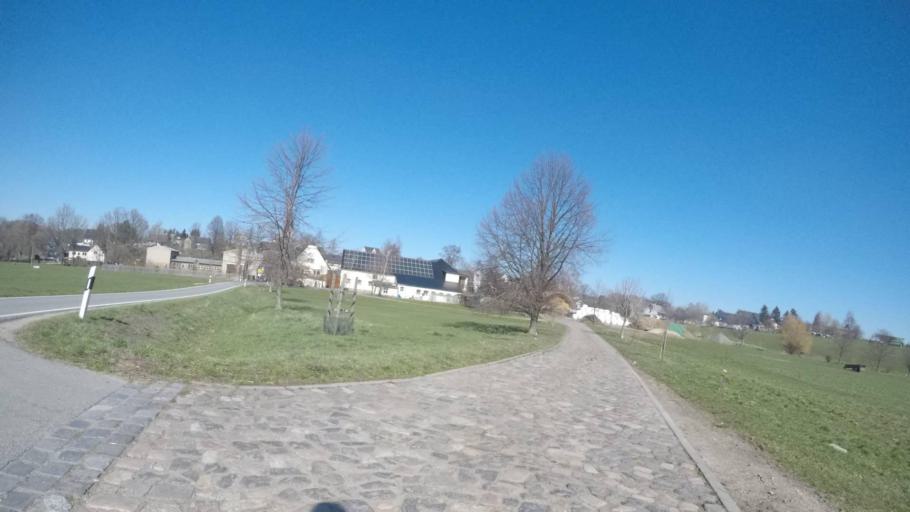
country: DE
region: Saxony
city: Niederfrohna
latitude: 50.8693
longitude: 12.6940
